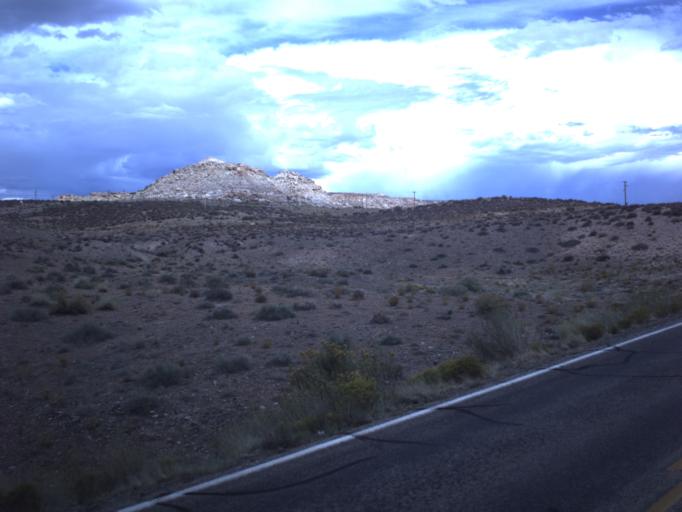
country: US
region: Utah
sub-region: San Juan County
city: Blanding
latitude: 37.2392
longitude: -109.2385
